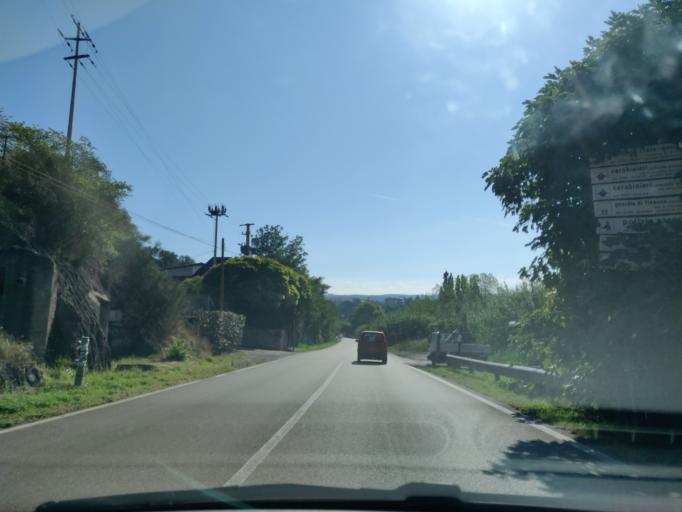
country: IT
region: Latium
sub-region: Provincia di Viterbo
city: Viterbo
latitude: 42.4159
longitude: 12.0920
